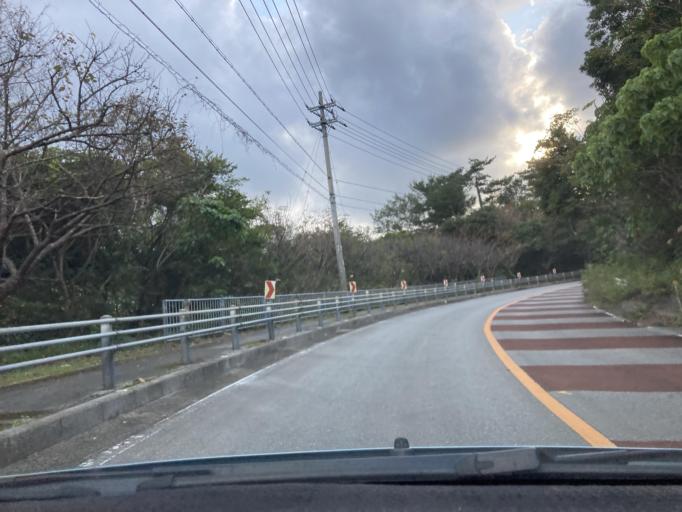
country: JP
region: Okinawa
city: Nago
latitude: 26.8313
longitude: 128.2845
